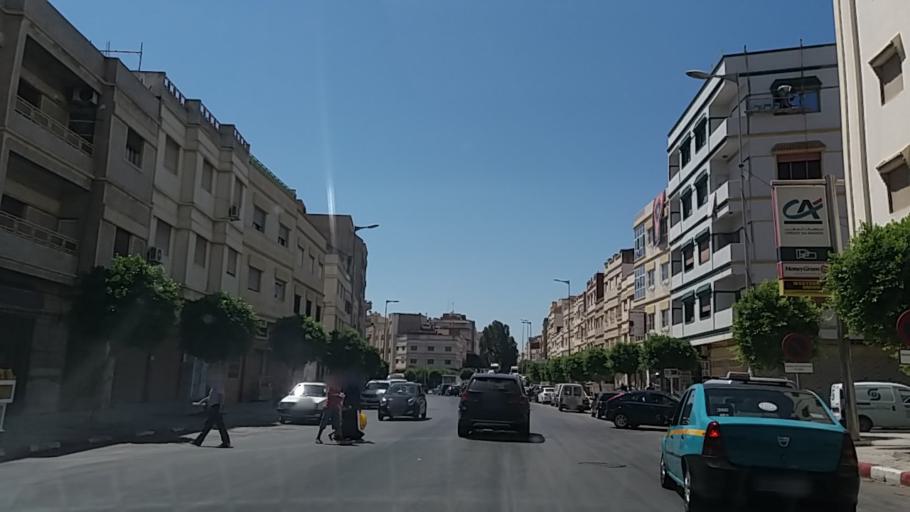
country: MA
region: Tanger-Tetouan
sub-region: Tanger-Assilah
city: Tangier
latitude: 35.7572
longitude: -5.8014
